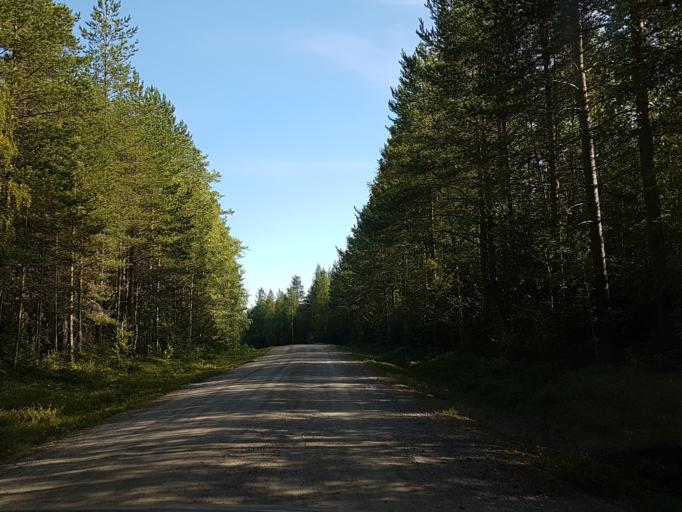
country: SE
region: Vaesterbotten
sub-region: Robertsfors Kommun
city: Robertsfors
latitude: 64.0513
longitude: 20.8717
